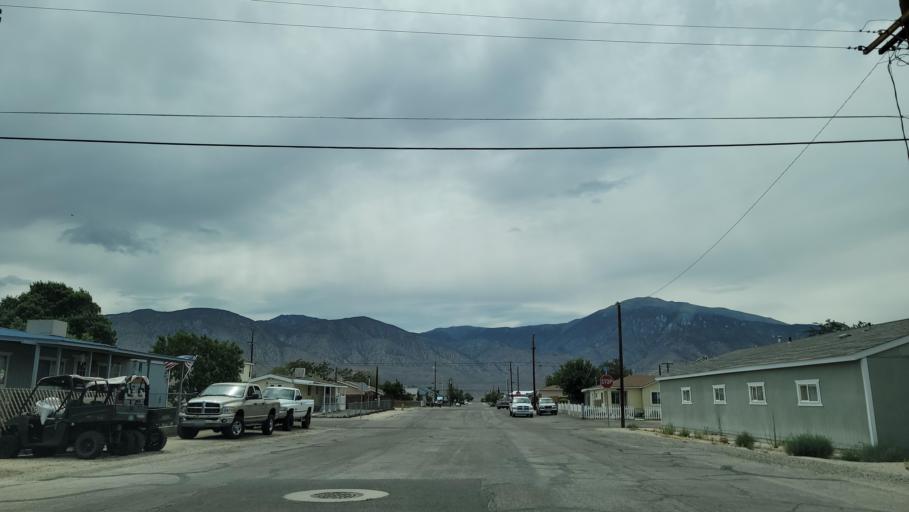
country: US
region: Nevada
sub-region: Mineral County
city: Hawthorne
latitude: 38.5308
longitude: -118.6222
